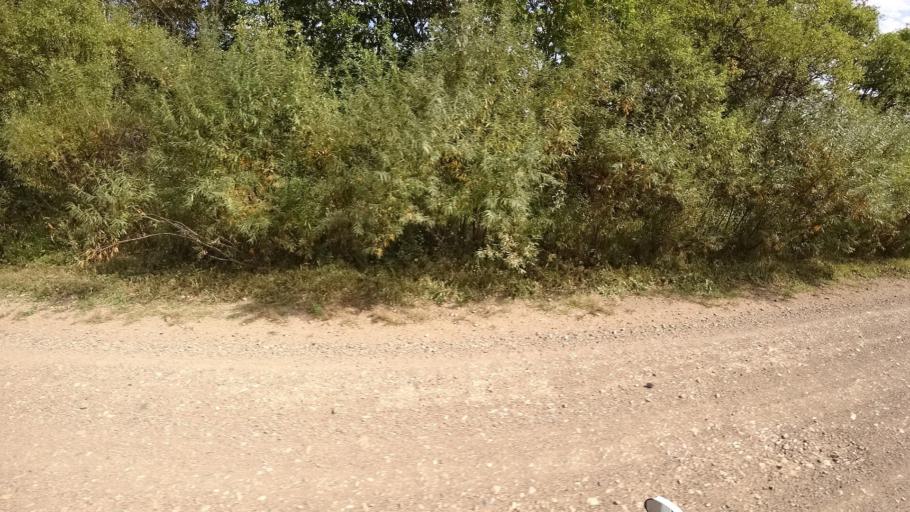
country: RU
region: Primorskiy
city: Yakovlevka
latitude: 44.7136
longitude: 133.6199
